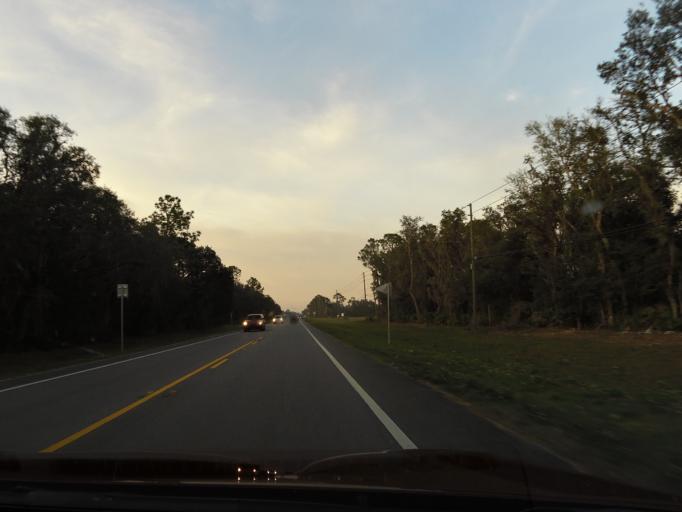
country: US
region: Florida
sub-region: Volusia County
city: North DeLand
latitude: 29.0957
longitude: -81.2961
